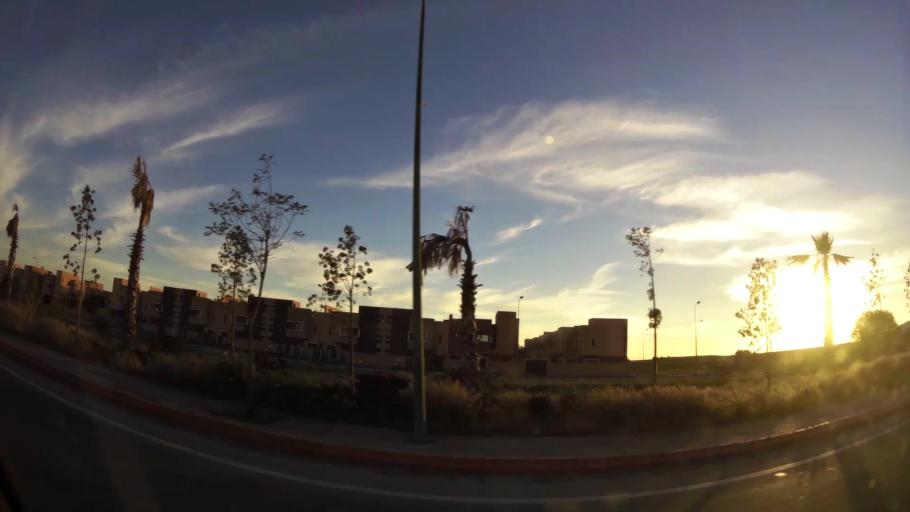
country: MA
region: Marrakech-Tensift-Al Haouz
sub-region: Marrakech
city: Marrakesh
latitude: 31.7641
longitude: -8.1179
